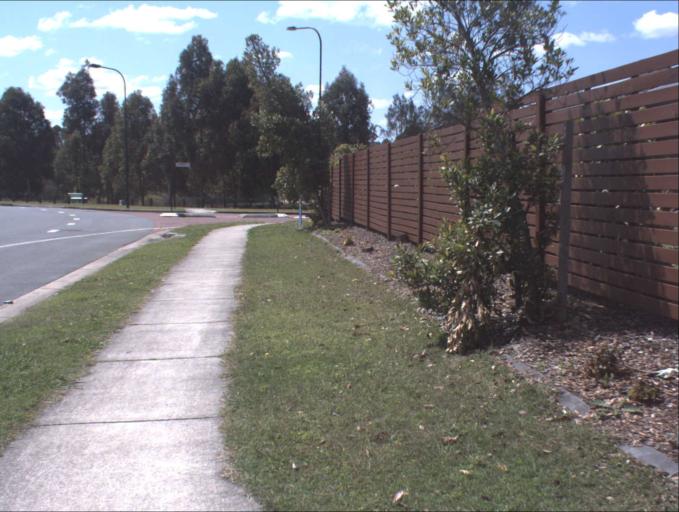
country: AU
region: Queensland
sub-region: Logan
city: Woodridge
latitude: -27.6586
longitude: 153.0756
